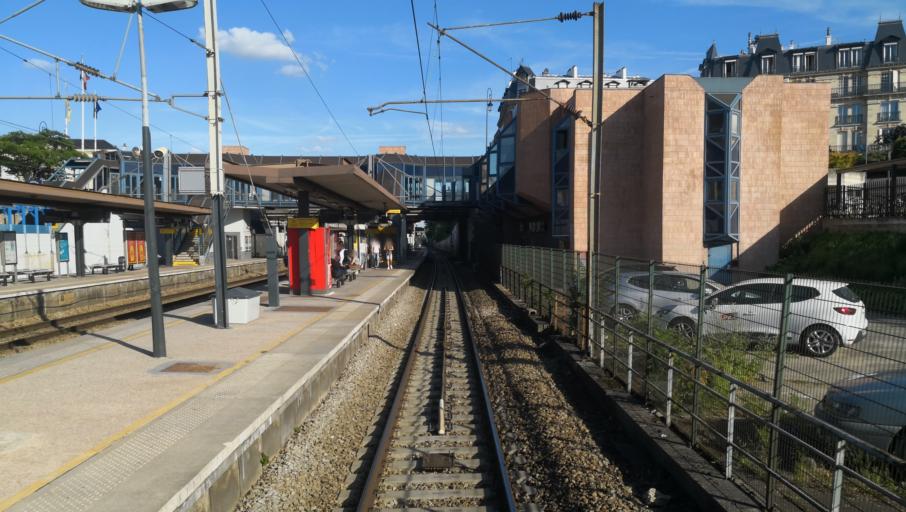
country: FR
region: Ile-de-France
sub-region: Departement des Yvelines
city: Maisons-Laffitte
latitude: 48.9462
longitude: 2.1438
